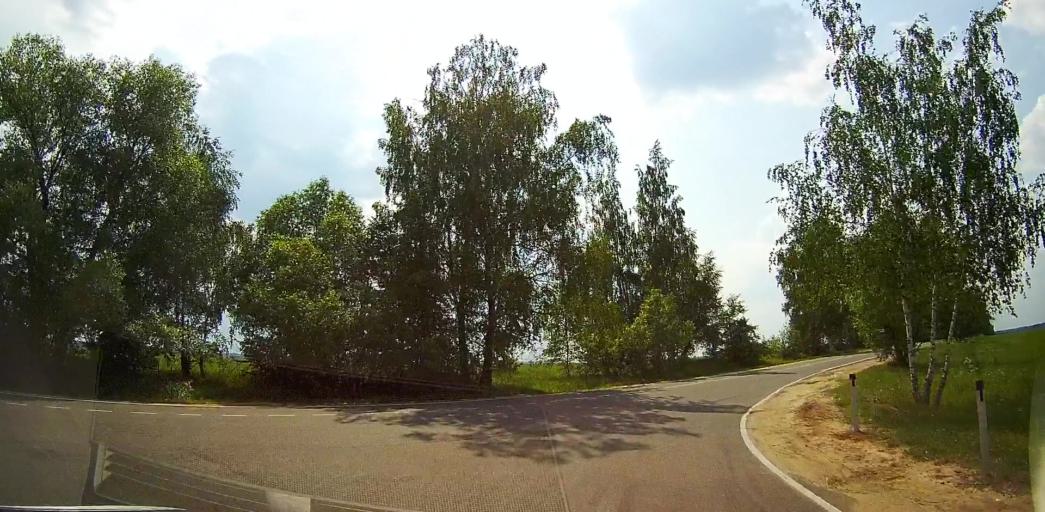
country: RU
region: Moskovskaya
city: Zhilevo
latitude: 55.0558
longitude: 38.0785
